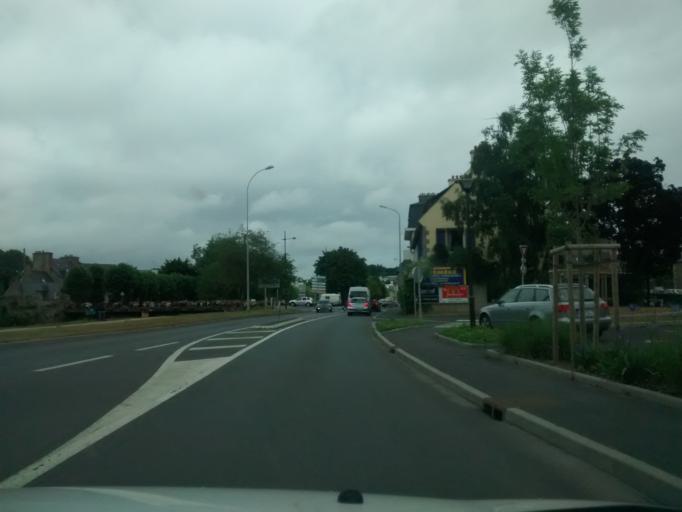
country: FR
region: Brittany
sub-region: Departement des Cotes-d'Armor
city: Lannion
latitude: 48.7273
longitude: -3.4570
